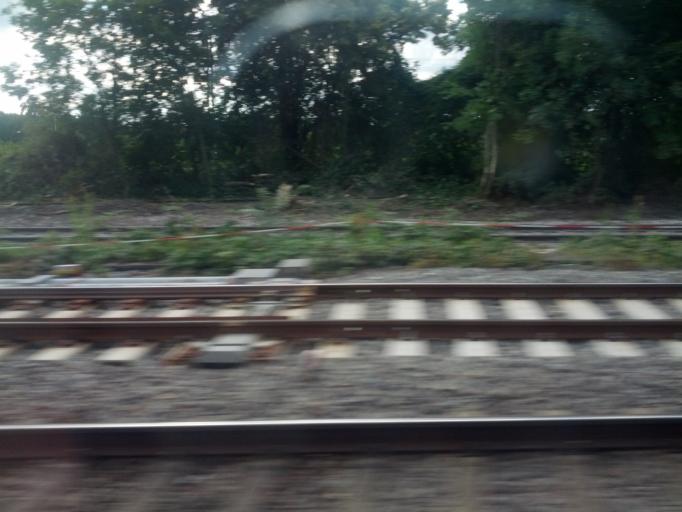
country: DE
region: Baden-Wuerttemberg
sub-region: Karlsruhe Region
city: Bruchsal
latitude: 49.1315
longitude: 8.5940
